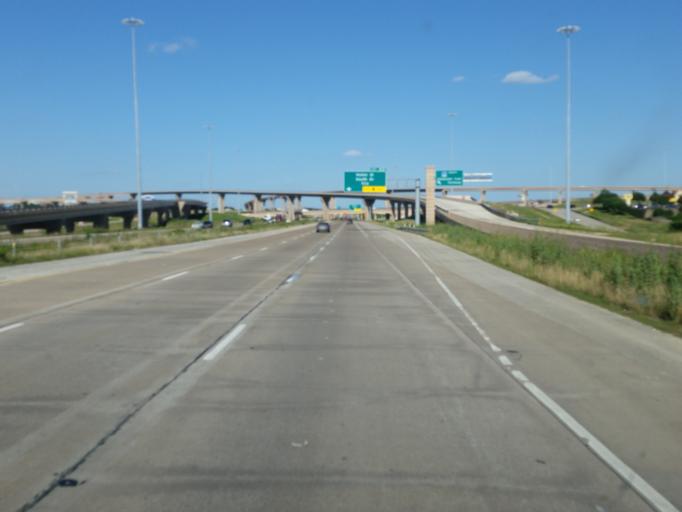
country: US
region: Texas
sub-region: Tarrant County
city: Benbrook
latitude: 32.6834
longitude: -97.4130
